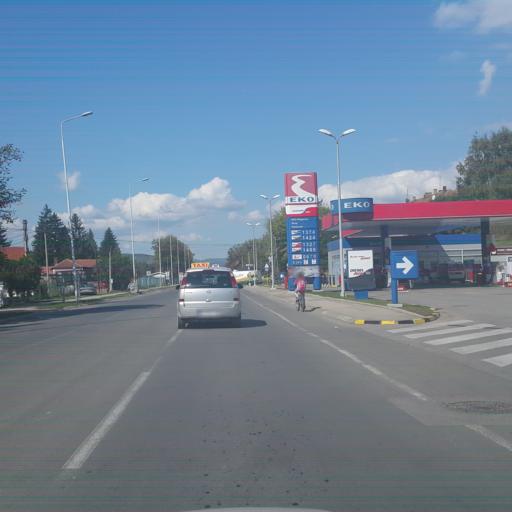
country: RS
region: Central Serbia
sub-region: Pirotski Okrug
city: Pirot
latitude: 43.1697
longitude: 22.5855
